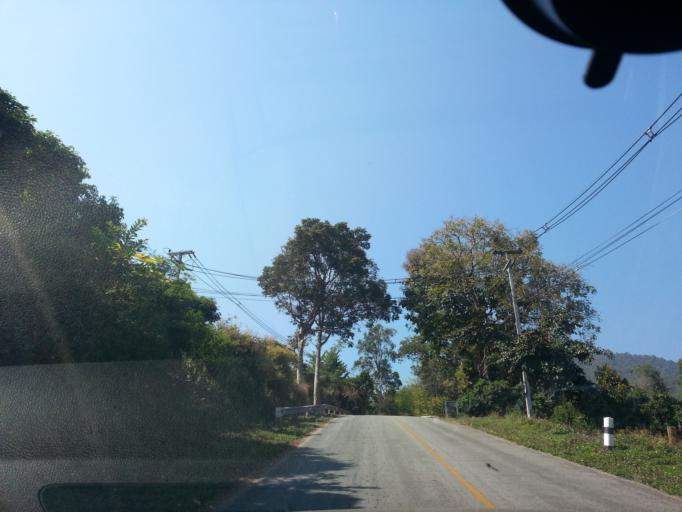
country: TH
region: Chiang Mai
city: Chai Prakan
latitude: 19.8329
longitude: 99.0991
